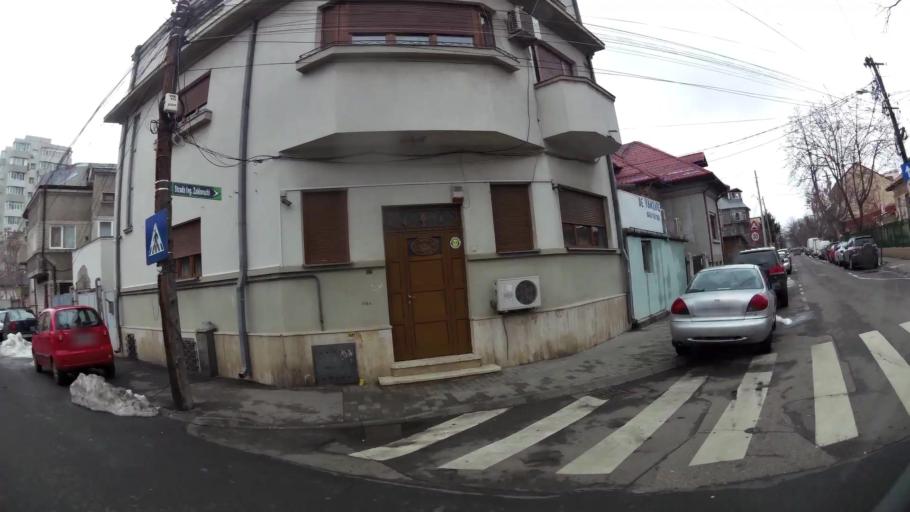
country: RO
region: Bucuresti
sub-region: Municipiul Bucuresti
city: Bucuresti
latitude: 44.4572
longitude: 26.0699
